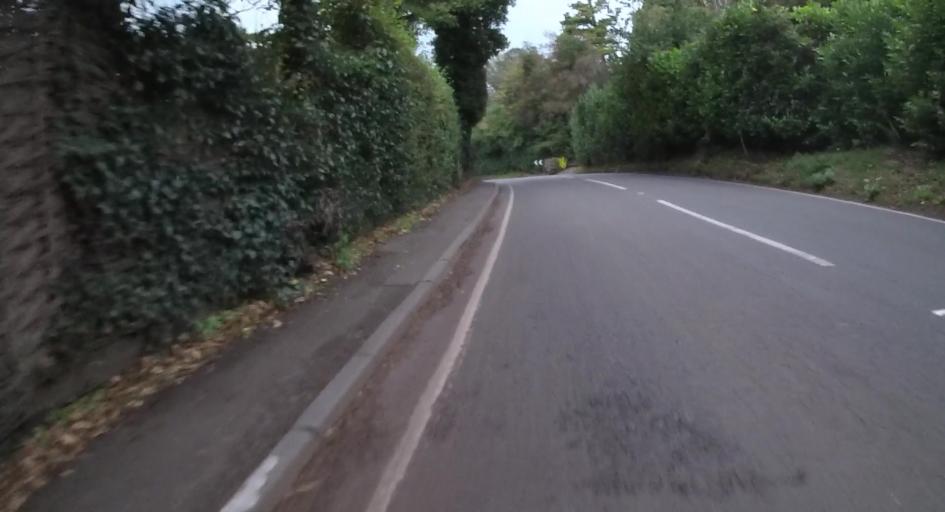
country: GB
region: England
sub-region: Wokingham
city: Finchampstead
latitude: 51.3658
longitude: -0.8506
